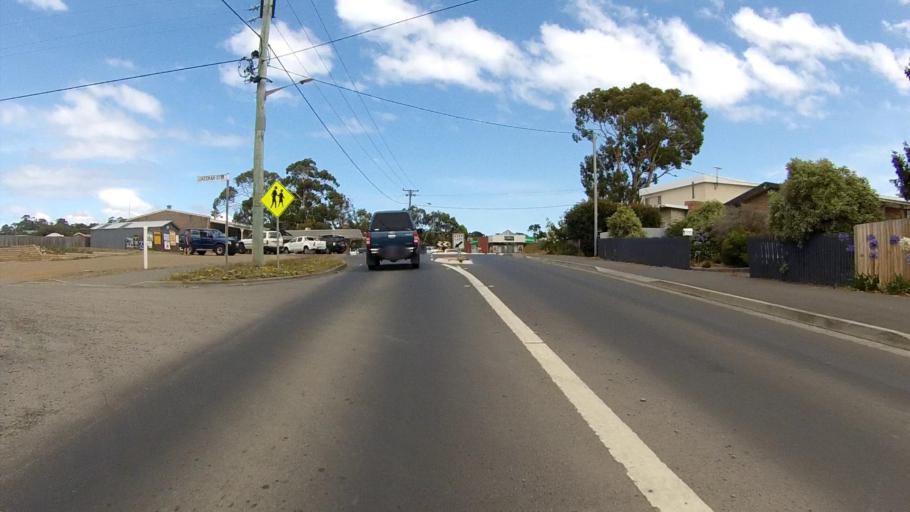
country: AU
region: Tasmania
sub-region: Sorell
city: Sorell
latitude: -42.8571
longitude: 147.6180
